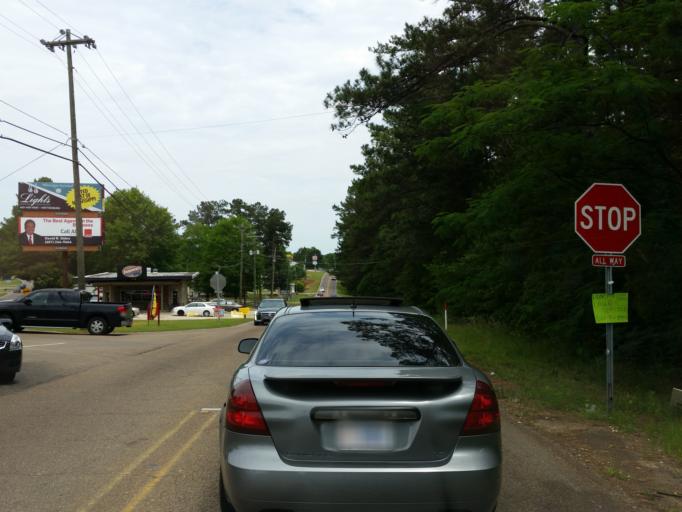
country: US
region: Mississippi
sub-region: Lamar County
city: West Hattiesburg
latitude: 31.3080
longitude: -89.3728
